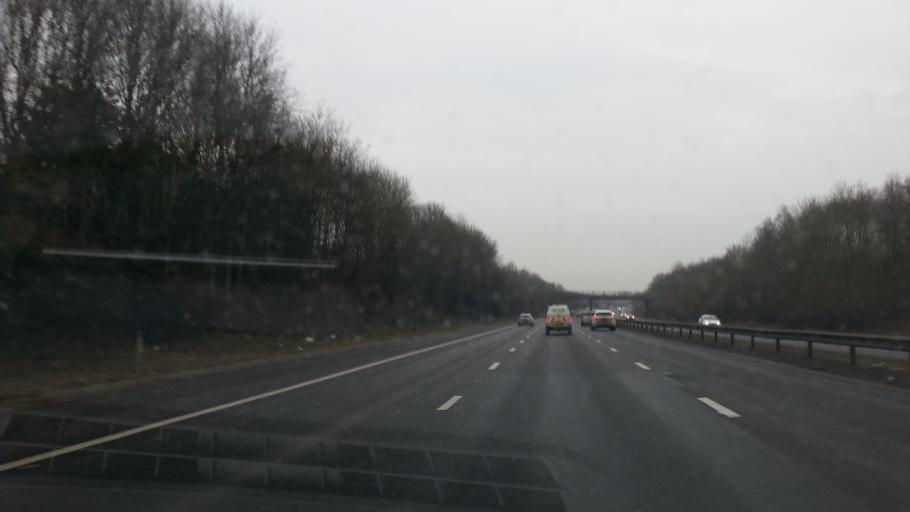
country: GB
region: England
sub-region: Essex
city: Harlow
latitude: 51.7553
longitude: 0.1464
